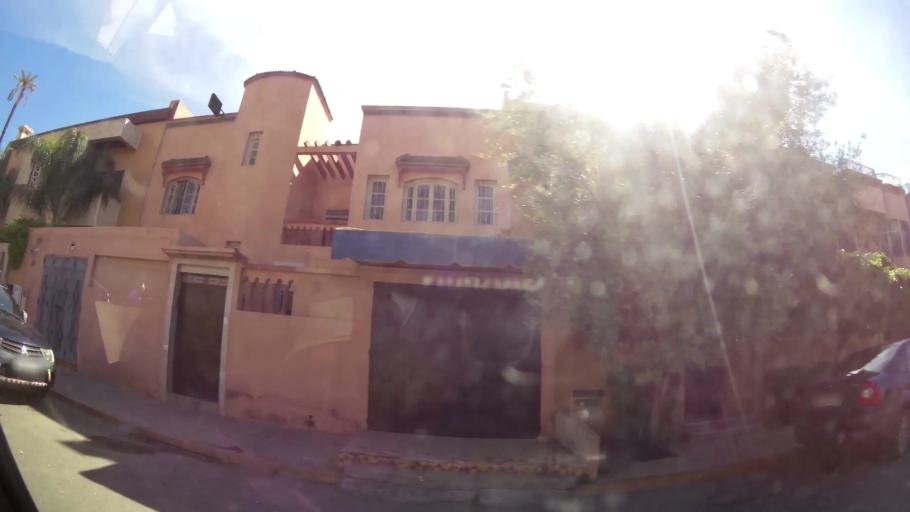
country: MA
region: Marrakech-Tensift-Al Haouz
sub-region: Marrakech
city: Marrakesh
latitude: 31.6641
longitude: -8.0285
